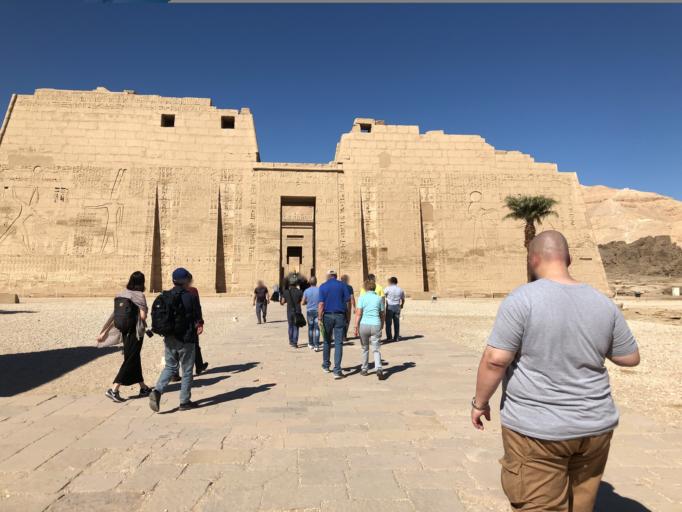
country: EG
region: Luxor
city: Luxor
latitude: 25.7190
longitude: 32.6016
